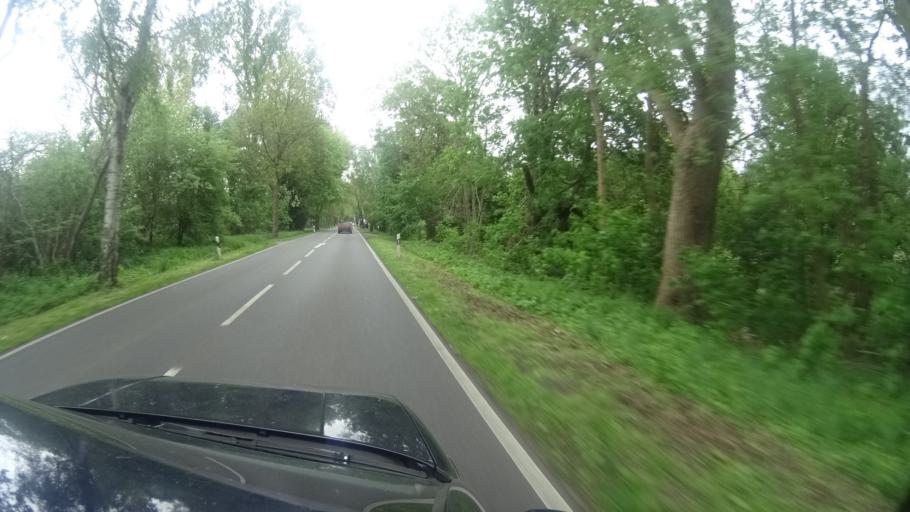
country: DE
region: Brandenburg
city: Fehrbellin
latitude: 52.8220
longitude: 12.7712
